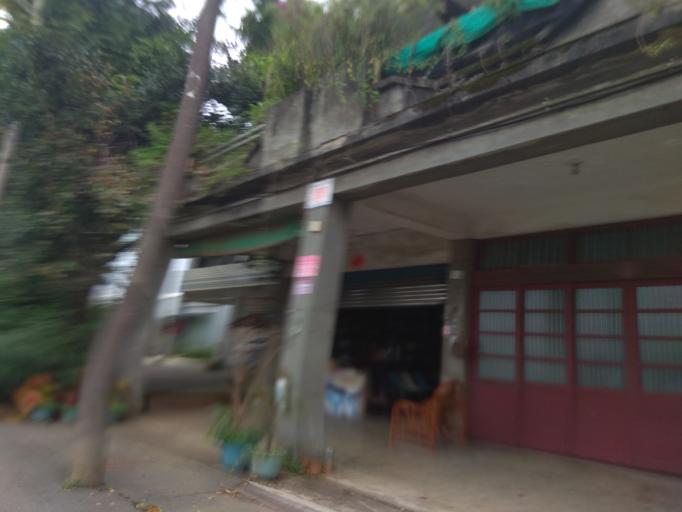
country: TW
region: Taiwan
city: Taoyuan City
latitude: 24.9930
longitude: 121.2214
